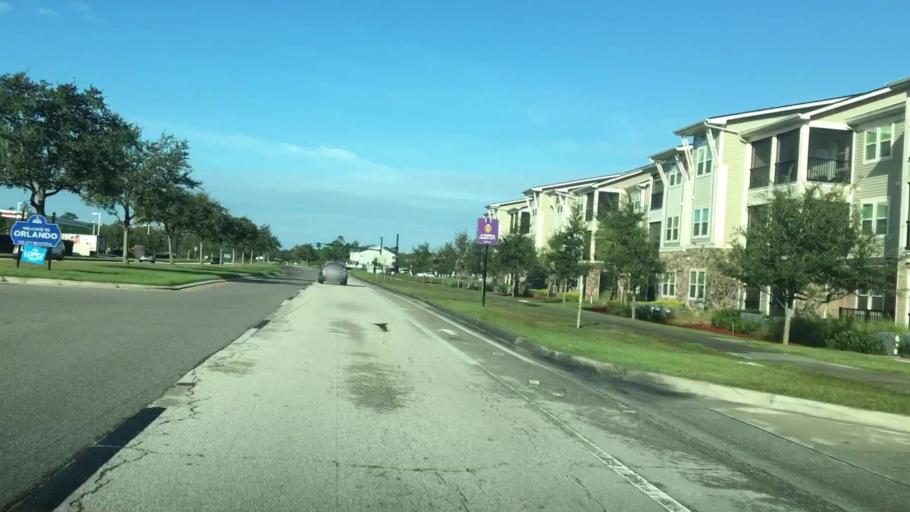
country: US
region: Florida
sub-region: Orange County
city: Azalea Park
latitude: 28.4783
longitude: -81.2447
